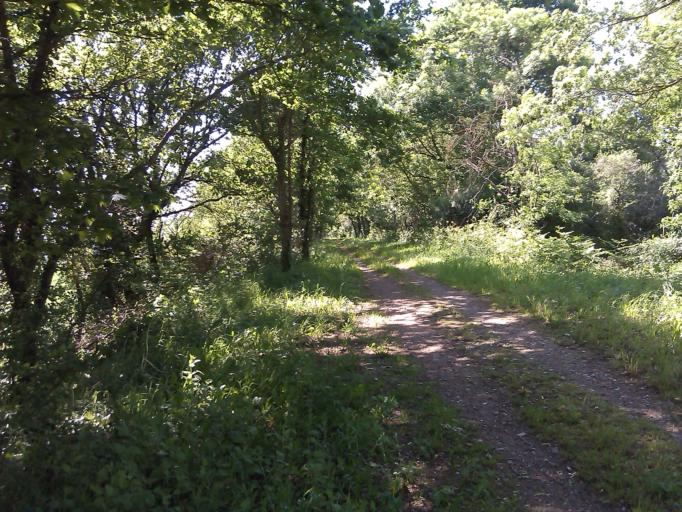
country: FR
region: Centre
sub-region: Departement de l'Indre
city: Saint-Gaultier
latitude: 46.6353
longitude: 1.2718
